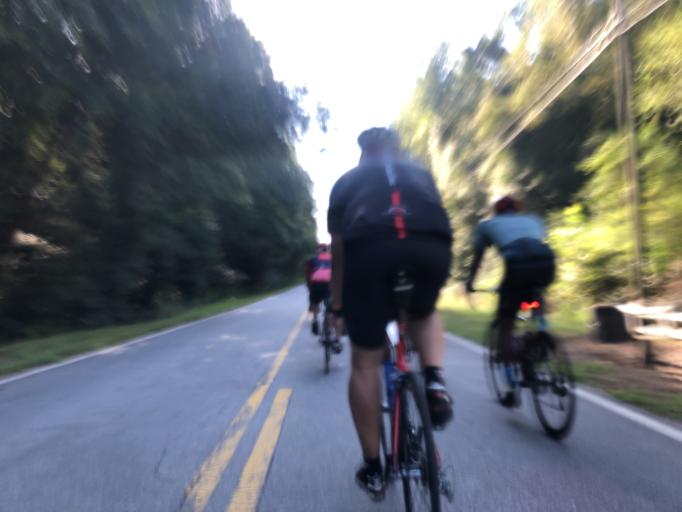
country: US
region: Georgia
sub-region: Fulton County
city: Chattahoochee Hills
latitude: 33.5499
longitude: -84.7652
